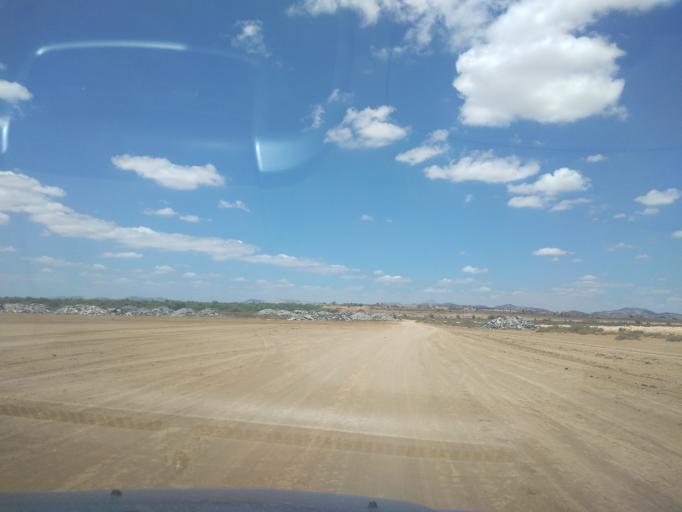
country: TN
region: Susah
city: Harqalah
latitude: 36.1642
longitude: 10.4520
